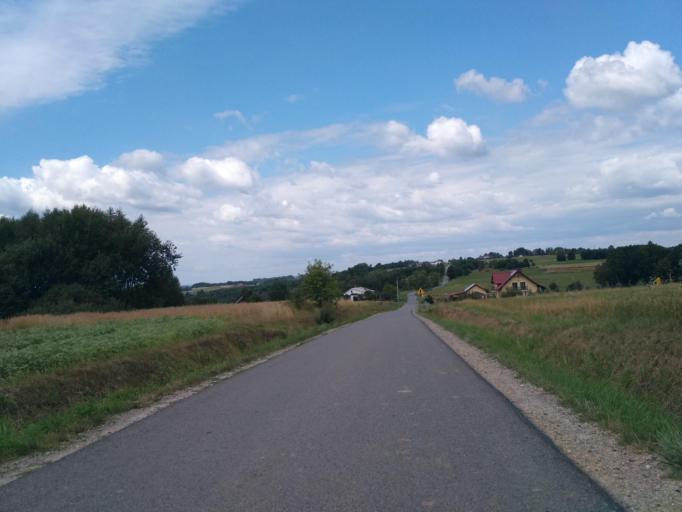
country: PL
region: Subcarpathian Voivodeship
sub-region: Powiat rzeszowski
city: Hyzne
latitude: 49.9097
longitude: 22.2215
